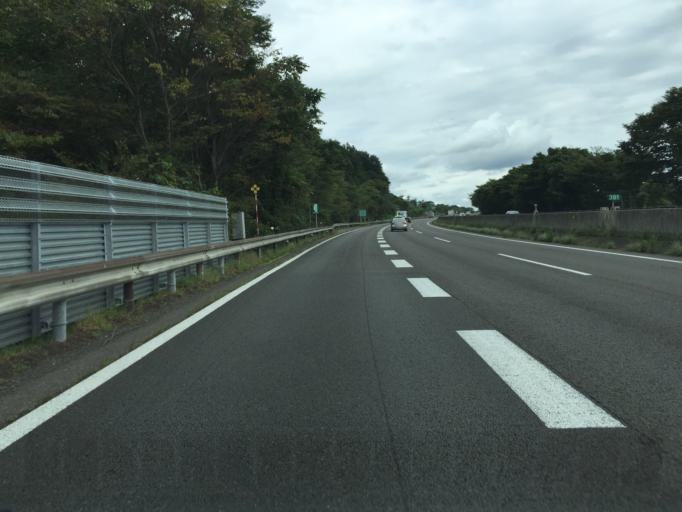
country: JP
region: Fukushima
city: Yanagawamachi-saiwaicho
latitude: 37.9025
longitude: 140.5708
